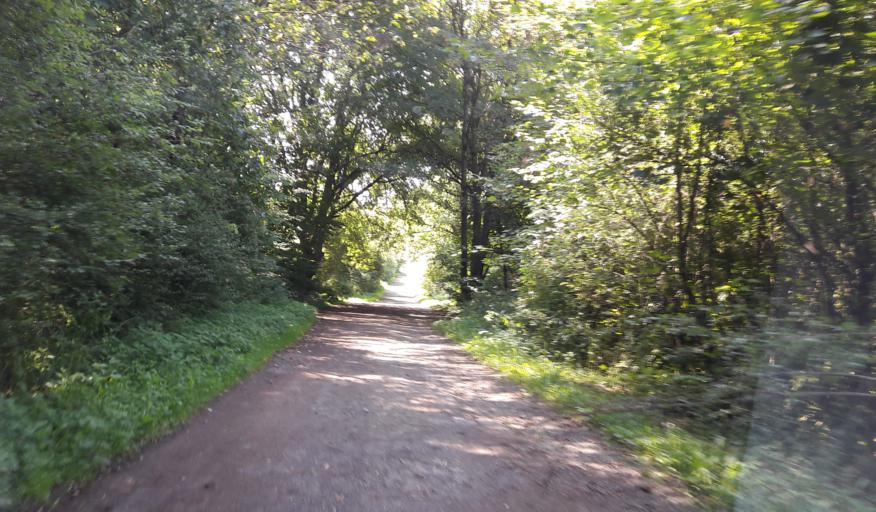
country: DE
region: Saarland
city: Mainzweiler
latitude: 49.4477
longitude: 7.1309
